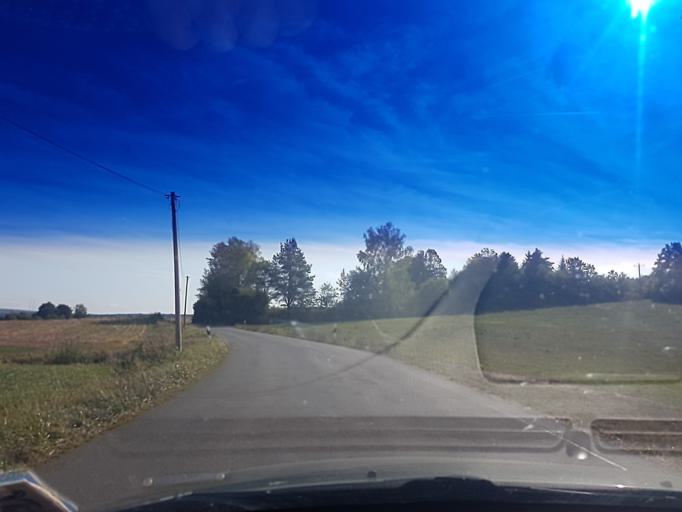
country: DE
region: Bavaria
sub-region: Upper Franconia
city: Schlusselfeld
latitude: 49.7791
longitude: 10.6016
